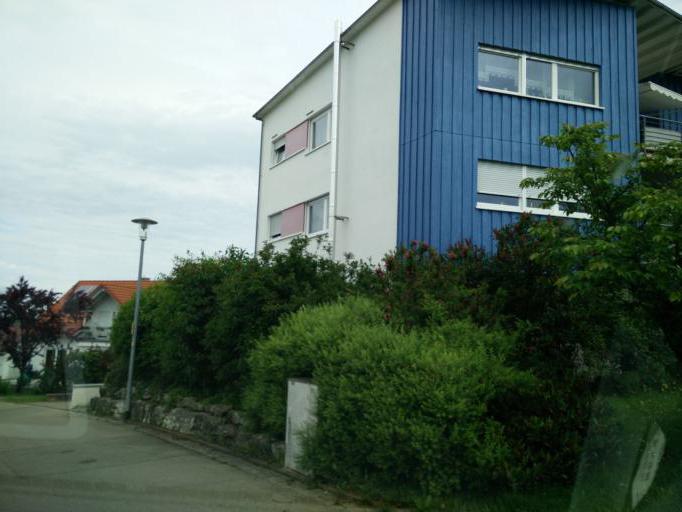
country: DE
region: Baden-Wuerttemberg
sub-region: Tuebingen Region
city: Gomaringen
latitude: 48.4594
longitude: 9.0889
